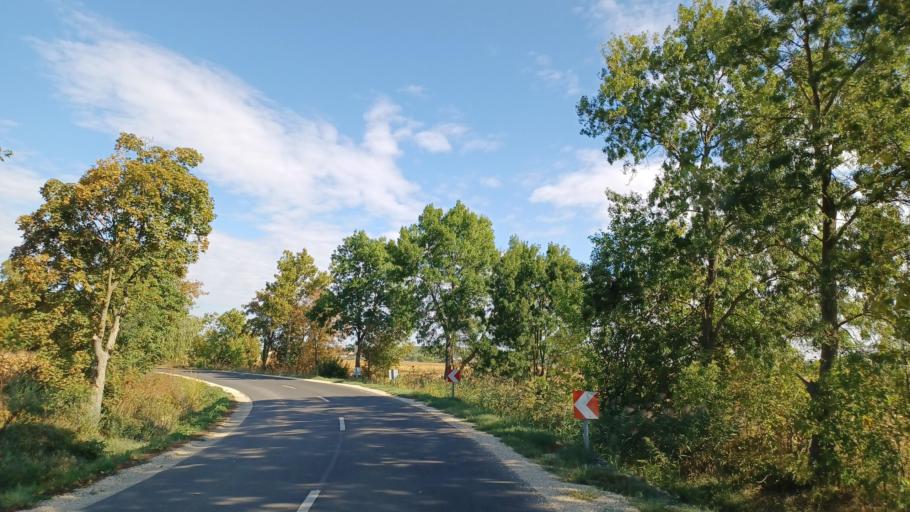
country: HU
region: Tolna
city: Dunaszentgyorgy
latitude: 46.5173
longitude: 18.8276
